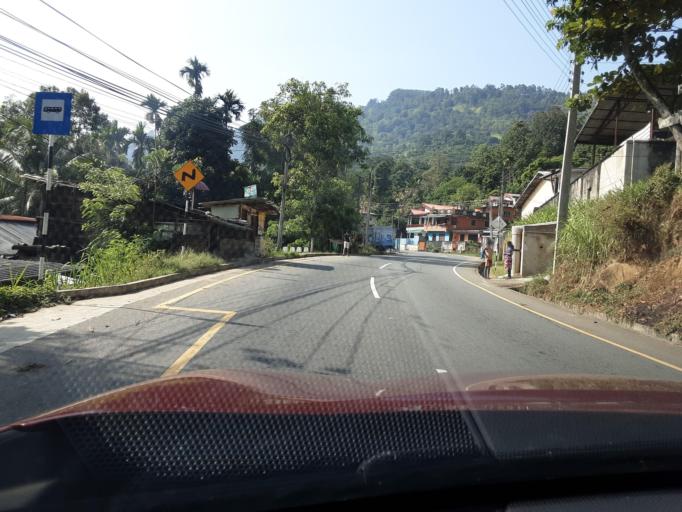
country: LK
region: Uva
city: Badulla
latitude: 6.9688
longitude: 81.0872
